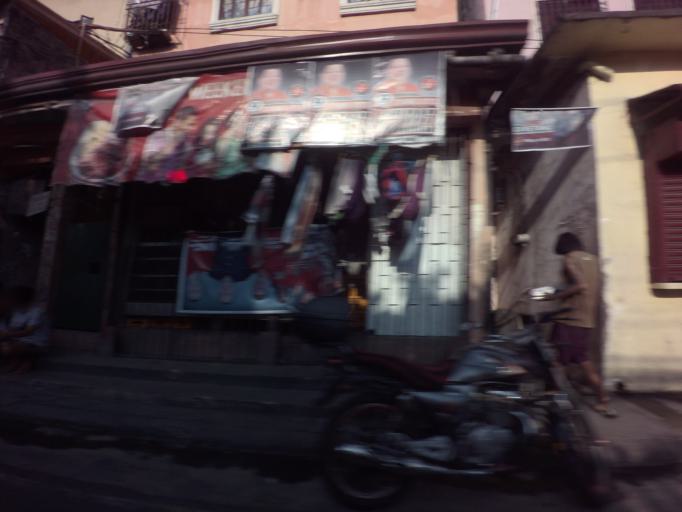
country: PH
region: Calabarzon
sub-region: Province of Rizal
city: Taguig
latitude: 14.4855
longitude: 121.0607
